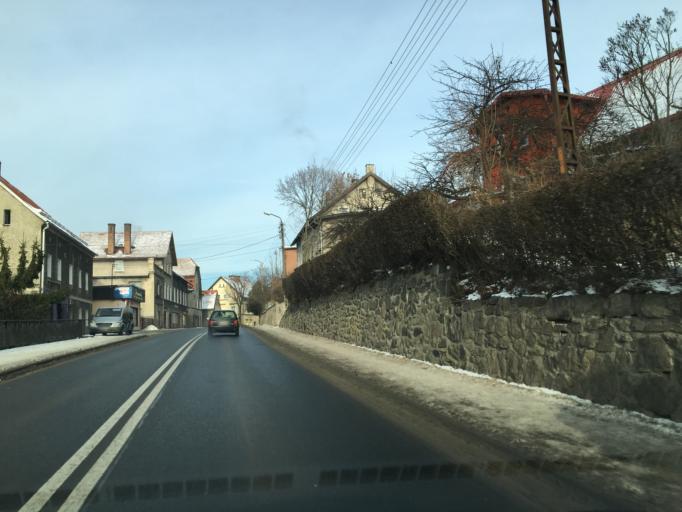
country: PL
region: Lower Silesian Voivodeship
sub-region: Powiat walbrzyski
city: Gluszyca
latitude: 50.6791
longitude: 16.3793
